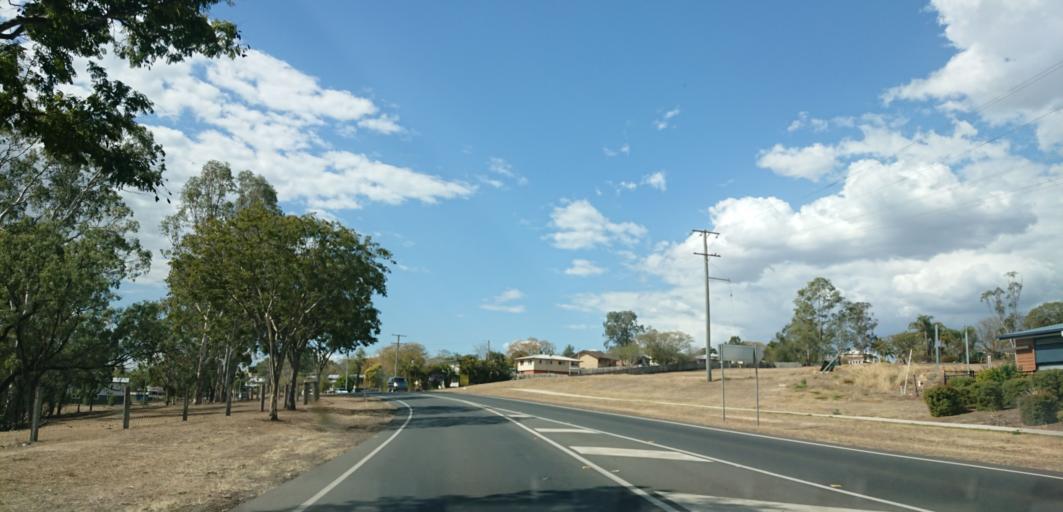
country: AU
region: Queensland
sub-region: Lockyer Valley
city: Gatton
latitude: -27.5684
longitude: 152.2704
